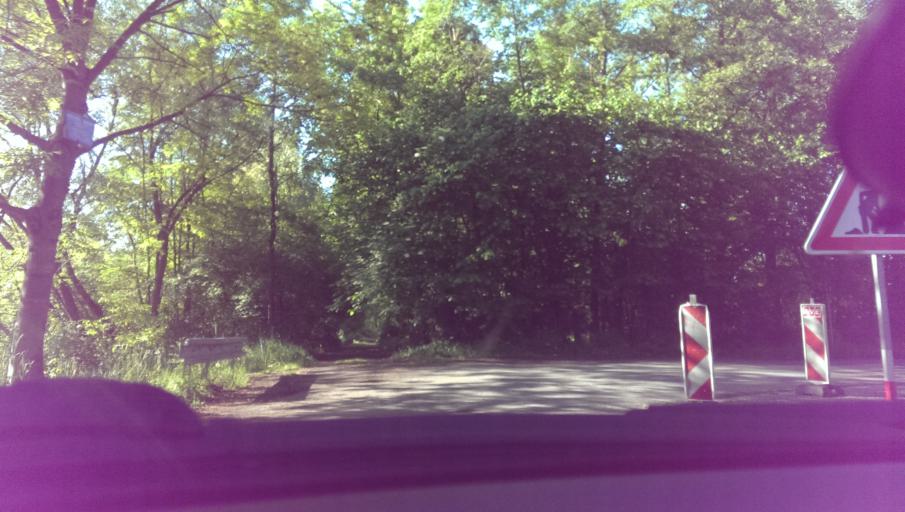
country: CZ
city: Frydlant nad Ostravici
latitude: 49.5805
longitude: 18.3655
